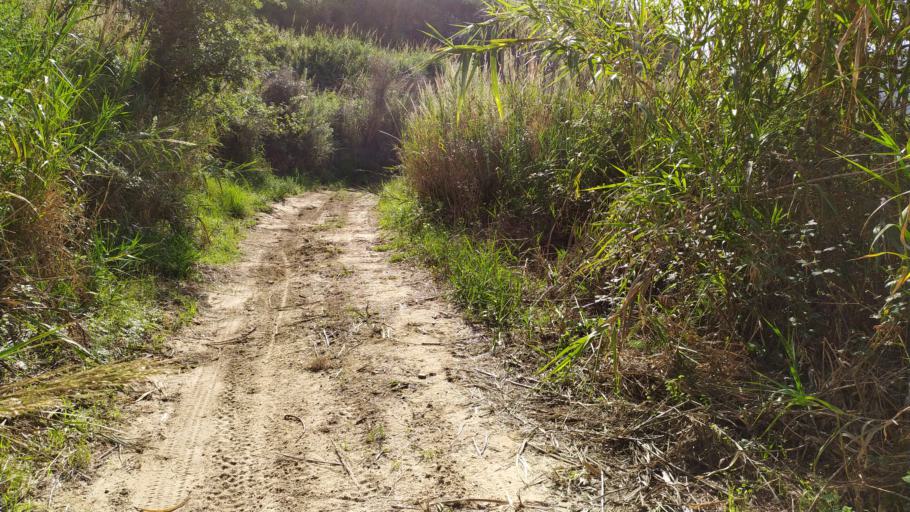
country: IT
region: Sicily
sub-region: Messina
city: Monforte San Giorgio
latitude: 38.1541
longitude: 15.3989
